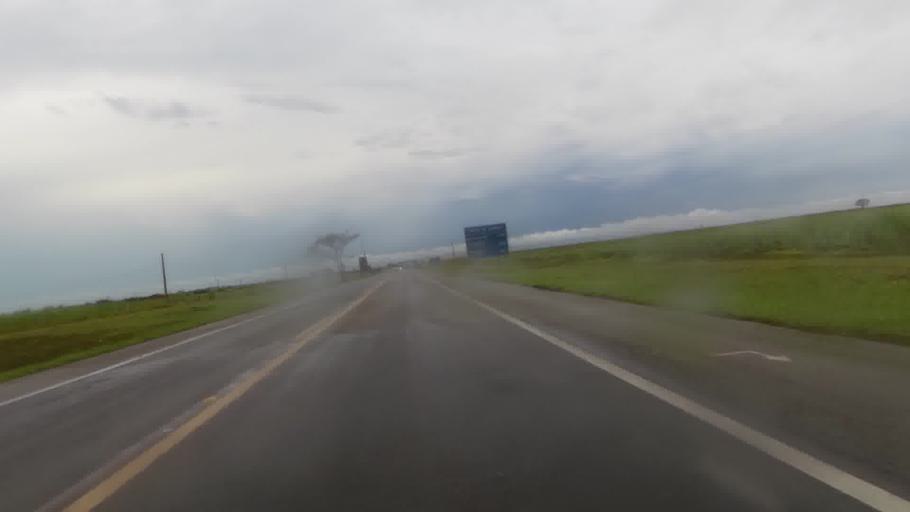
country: BR
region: Rio de Janeiro
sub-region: Campos Dos Goytacazes
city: Campos
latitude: -21.5483
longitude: -41.3365
